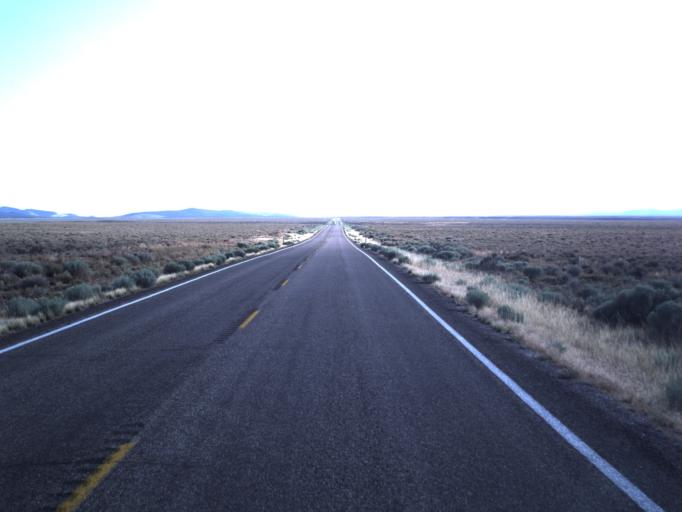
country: US
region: Utah
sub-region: Iron County
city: Enoch
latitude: 37.9299
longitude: -113.0293
